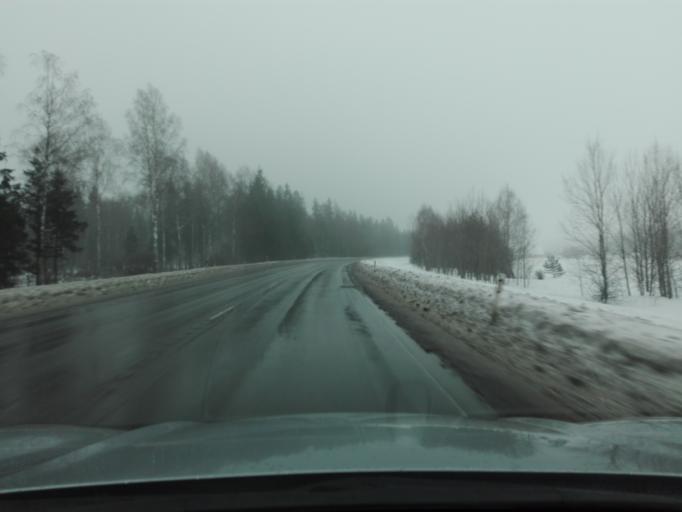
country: EE
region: Raplamaa
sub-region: Kohila vald
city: Kohila
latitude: 59.2282
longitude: 24.7767
